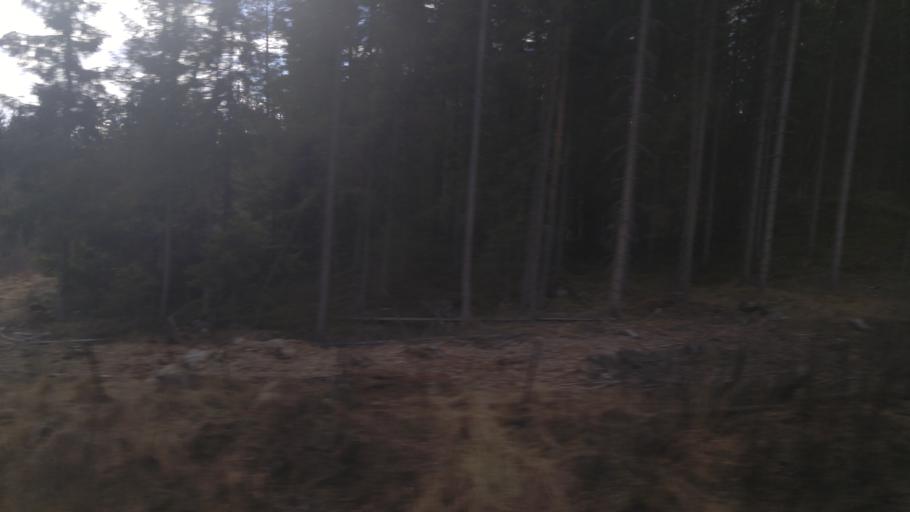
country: NO
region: Hedmark
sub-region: Stange
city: Stange
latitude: 60.6632
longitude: 11.2243
